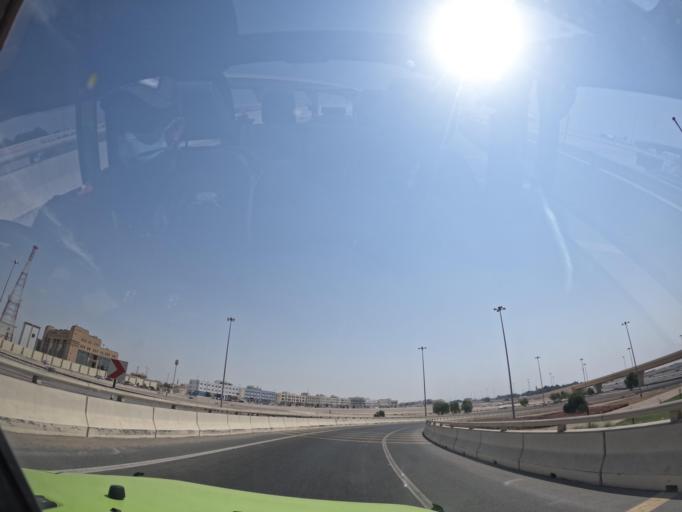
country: AE
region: Abu Dhabi
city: Abu Dhabi
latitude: 24.3101
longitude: 54.6032
